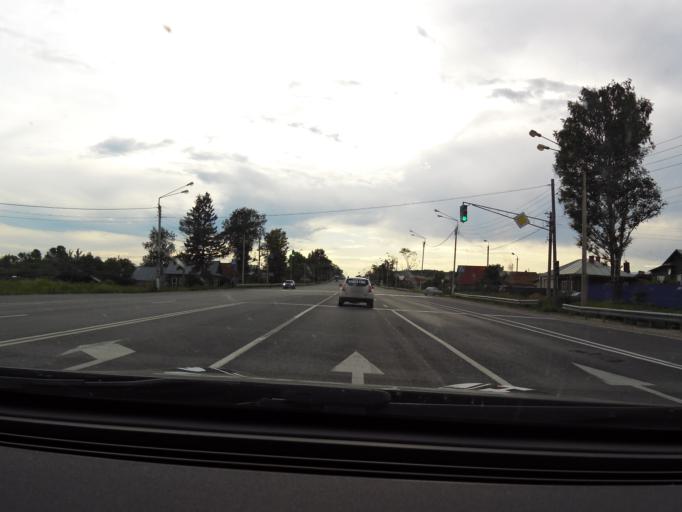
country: RU
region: Vladimir
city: Luknovo
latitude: 56.2392
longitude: 42.0700
